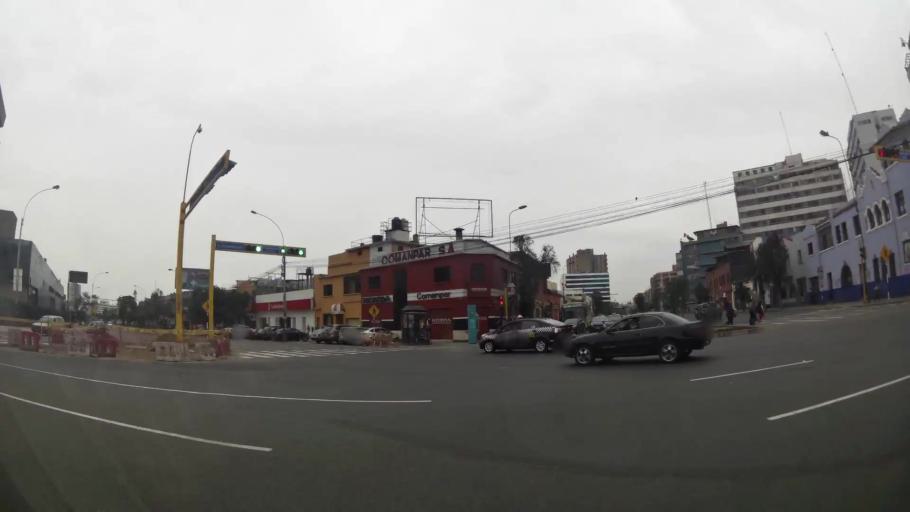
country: PE
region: Lima
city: Lima
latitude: -12.0645
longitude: -77.0394
